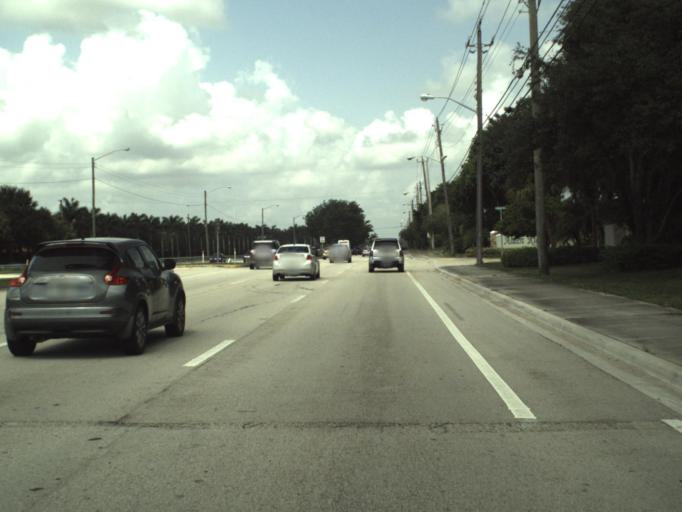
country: US
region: Florida
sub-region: Palm Beach County
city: Villages of Oriole
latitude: 26.5284
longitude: -80.1498
